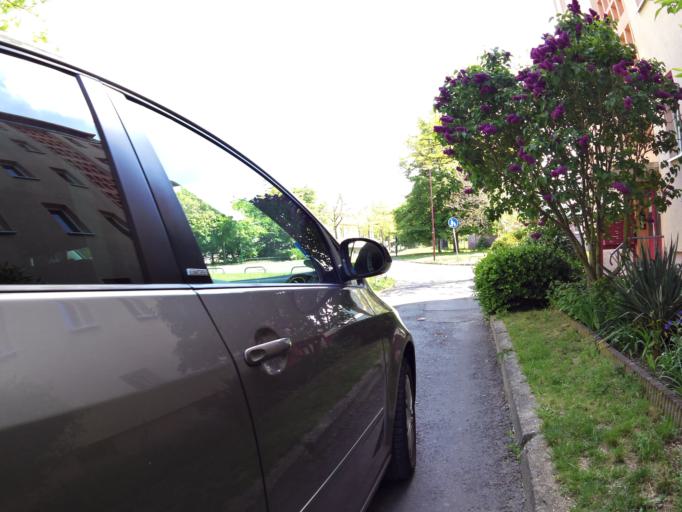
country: DE
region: Thuringia
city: Bad Salzungen
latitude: 50.8101
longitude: 10.2193
